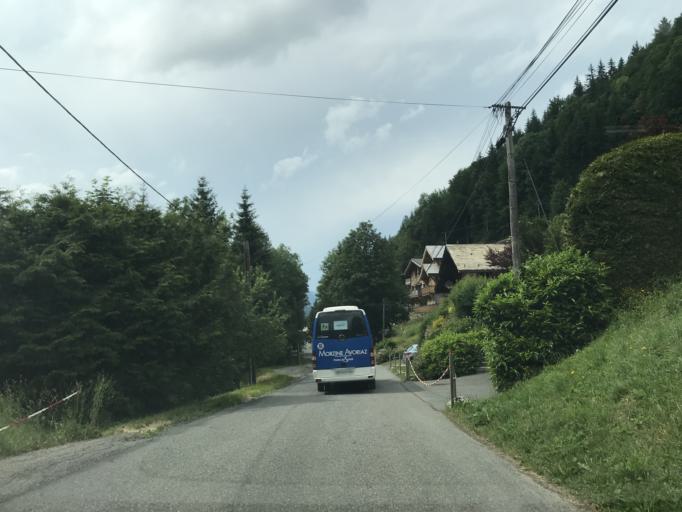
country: FR
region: Rhone-Alpes
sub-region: Departement de la Haute-Savoie
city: Morzine
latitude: 46.1641
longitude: 6.7205
